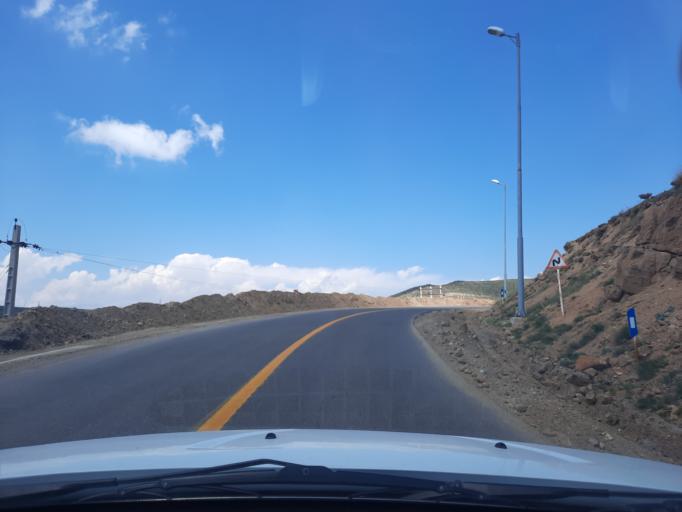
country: IR
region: Qazvin
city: Qazvin
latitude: 36.3872
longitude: 50.2072
